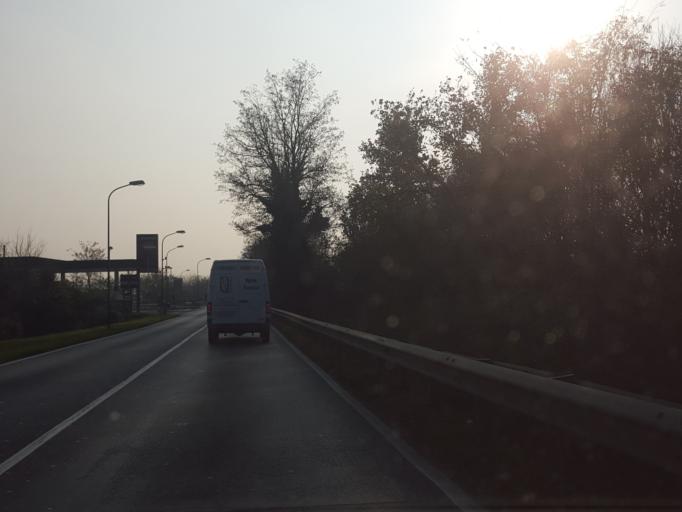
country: IT
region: Veneto
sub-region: Provincia di Treviso
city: Treviso
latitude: 45.6665
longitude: 12.2225
